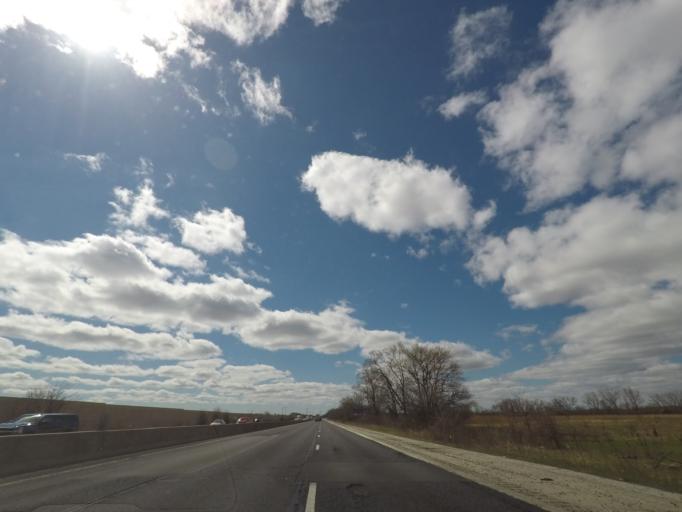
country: US
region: Illinois
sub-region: Will County
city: Crystal Lawns
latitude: 41.6082
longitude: -88.1634
